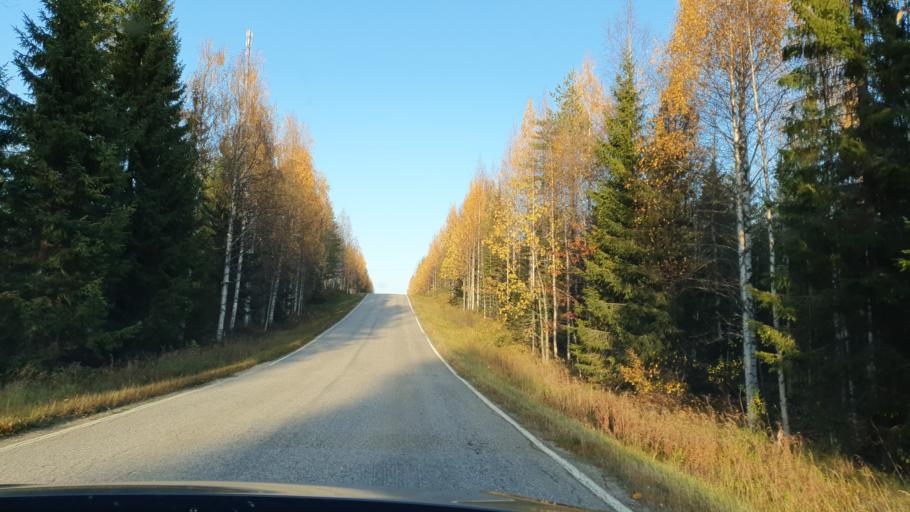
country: FI
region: Kainuu
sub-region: Kehys-Kainuu
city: Kuhmo
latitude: 64.3193
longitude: 29.4805
